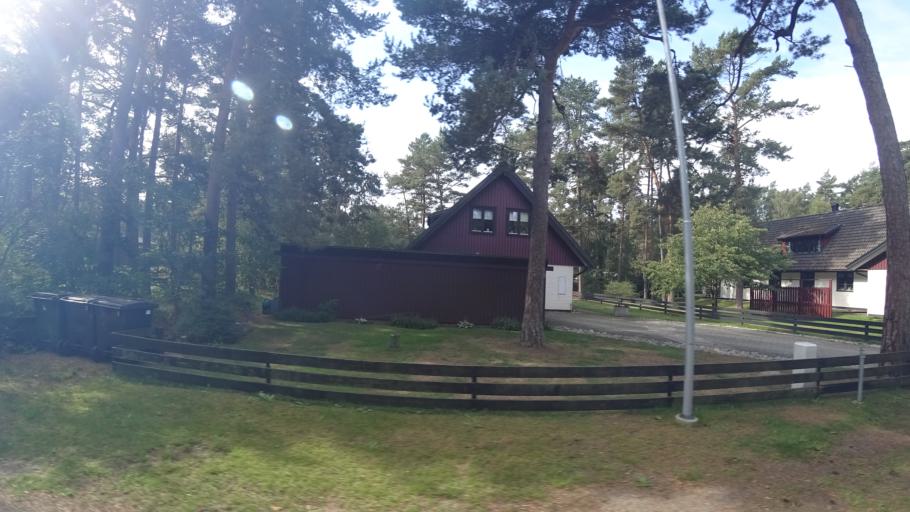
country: SE
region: Skane
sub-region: Kristianstads Kommun
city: Ahus
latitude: 55.9133
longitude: 14.3009
